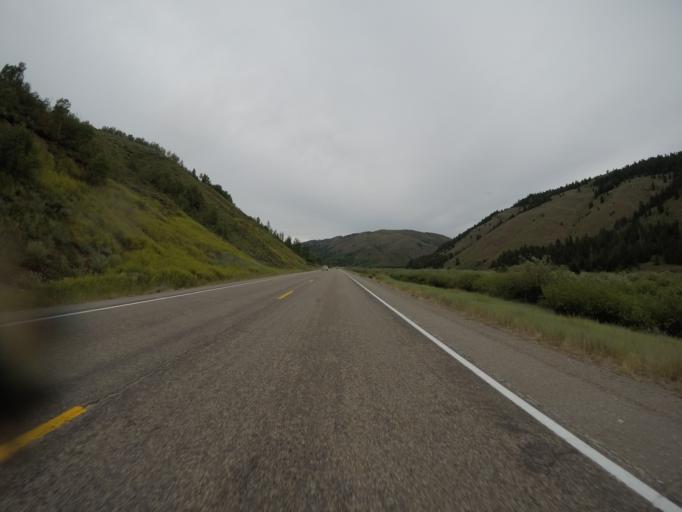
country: US
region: Wyoming
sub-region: Lincoln County
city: Afton
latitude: 42.4766
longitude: -110.9647
